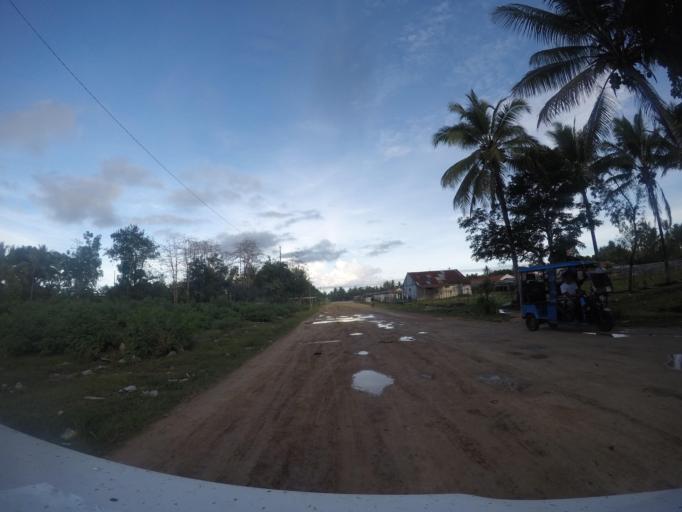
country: TL
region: Lautem
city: Lospalos
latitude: -8.5105
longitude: 127.0025
